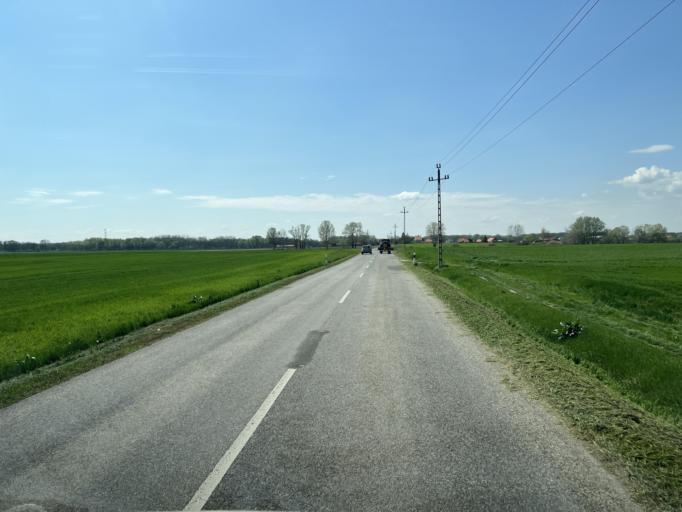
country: HU
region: Pest
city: Dabas
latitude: 47.2274
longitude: 19.3001
